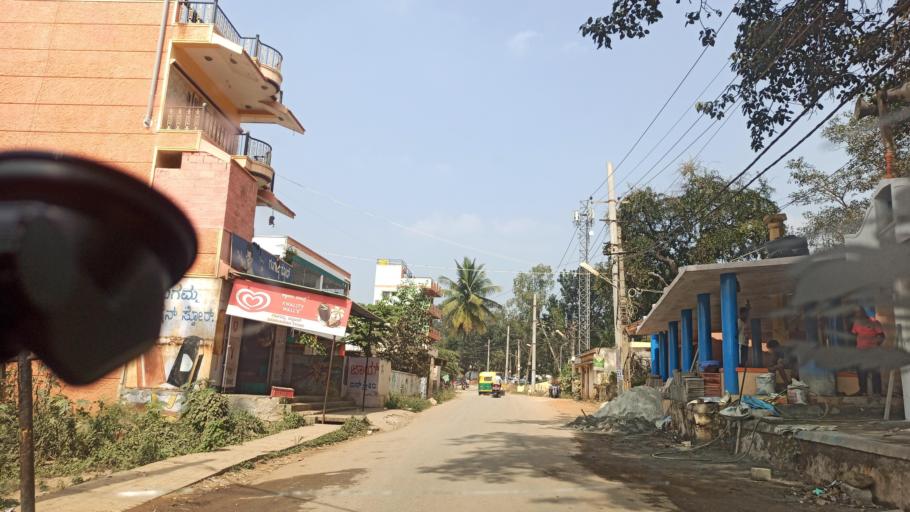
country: IN
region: Karnataka
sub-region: Bangalore Urban
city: Yelahanka
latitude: 13.0910
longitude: 77.6195
